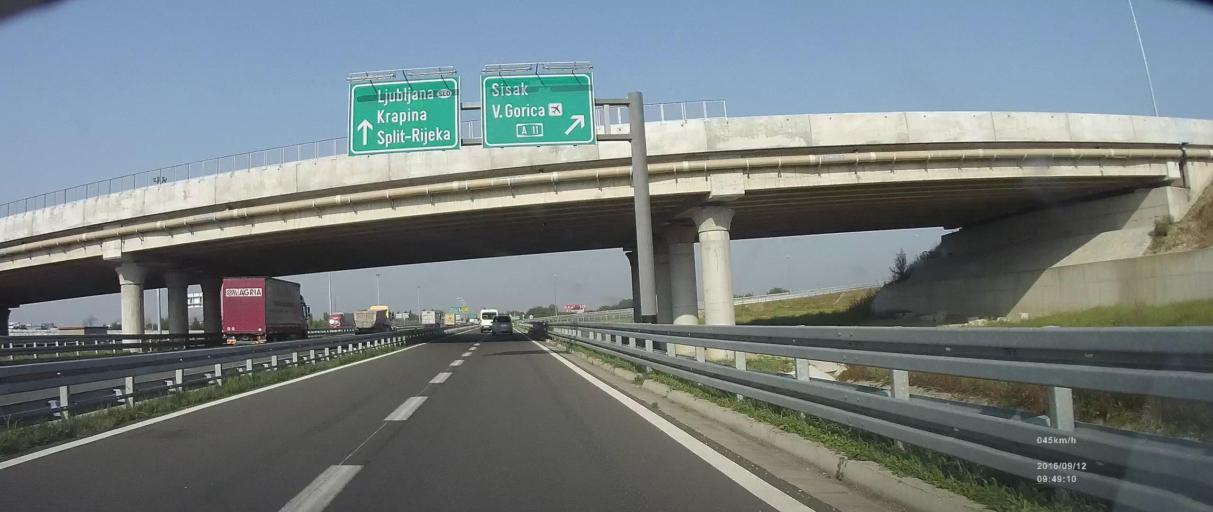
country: HR
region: Grad Zagreb
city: Odra
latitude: 45.7516
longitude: 16.0056
